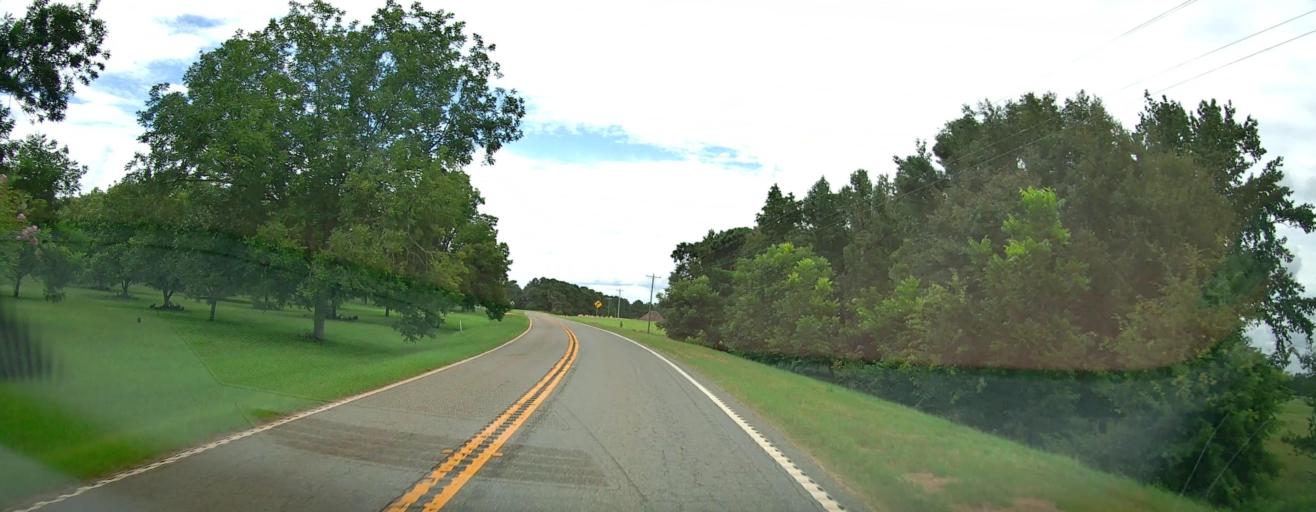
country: US
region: Georgia
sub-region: Dooly County
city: Unadilla
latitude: 32.2743
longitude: -83.8164
